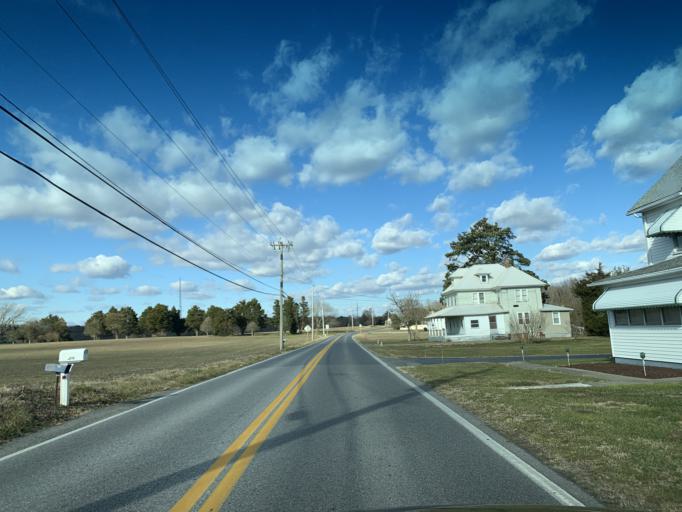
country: US
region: Maryland
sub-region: Worcester County
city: Berlin
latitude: 38.3347
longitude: -75.2210
